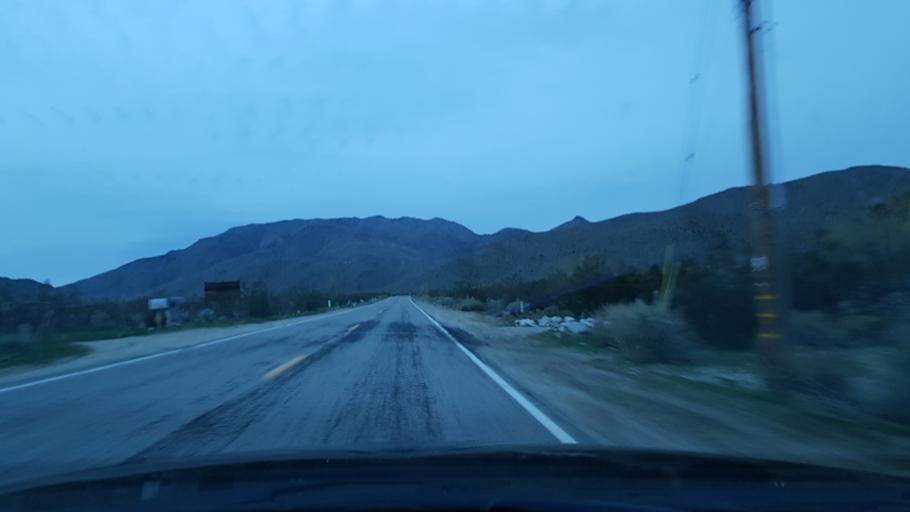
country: US
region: California
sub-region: San Diego County
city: Julian
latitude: 32.9923
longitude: -116.4458
